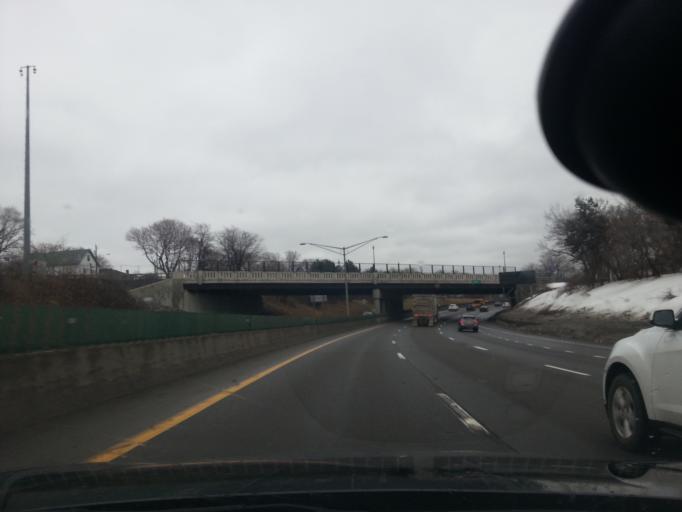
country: US
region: New York
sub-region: Onondaga County
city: Syracuse
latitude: 43.0654
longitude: -76.1614
